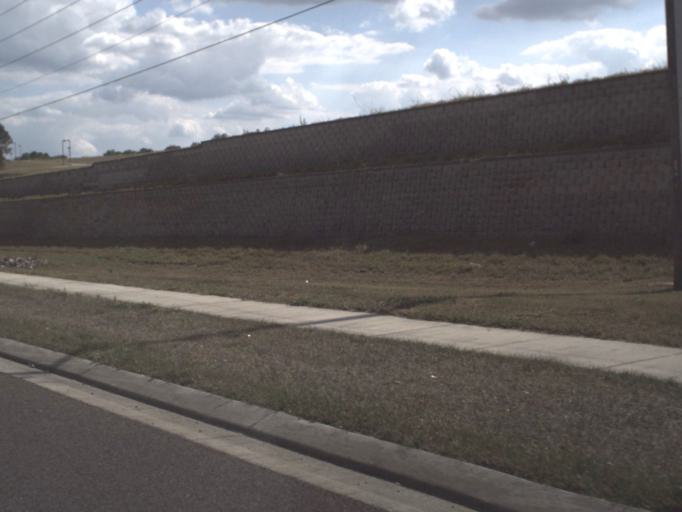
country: US
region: Florida
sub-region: Lake County
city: Clermont
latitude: 28.5166
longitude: -81.7268
